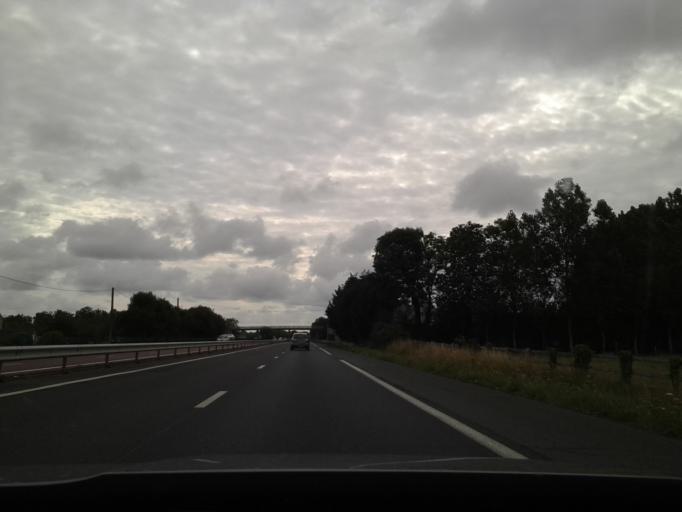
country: FR
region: Lower Normandy
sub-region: Departement du Calvados
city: Grandcamp-Maisy
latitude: 49.3425
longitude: -1.0444
